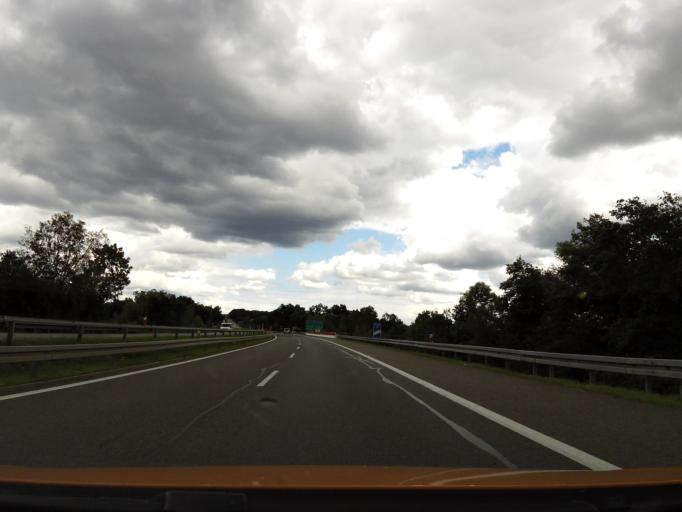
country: PL
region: West Pomeranian Voivodeship
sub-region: Powiat policki
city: Przeclaw
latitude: 53.3329
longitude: 14.5398
